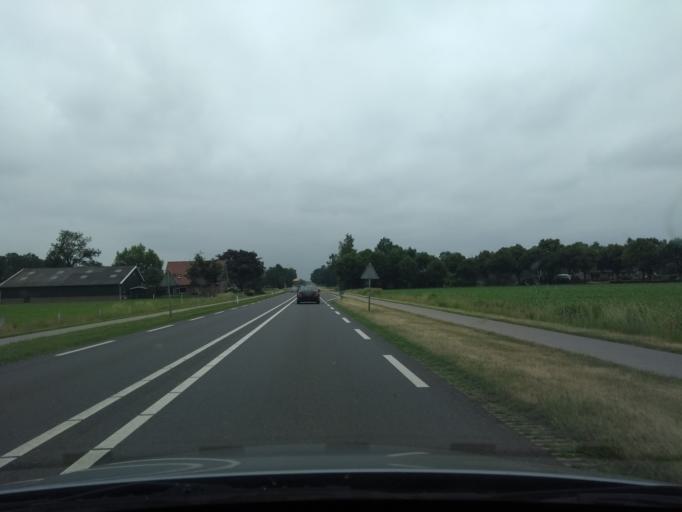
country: NL
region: Overijssel
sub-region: Gemeente Haaksbergen
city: Haaksbergen
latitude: 52.1911
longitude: 6.7359
